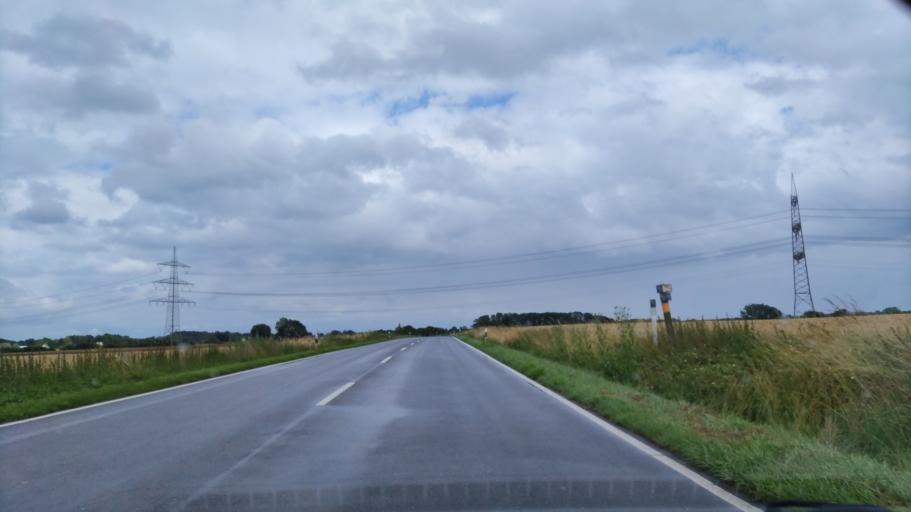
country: DE
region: North Rhine-Westphalia
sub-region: Regierungsbezirk Arnsberg
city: Welver
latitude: 51.6471
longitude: 7.9384
